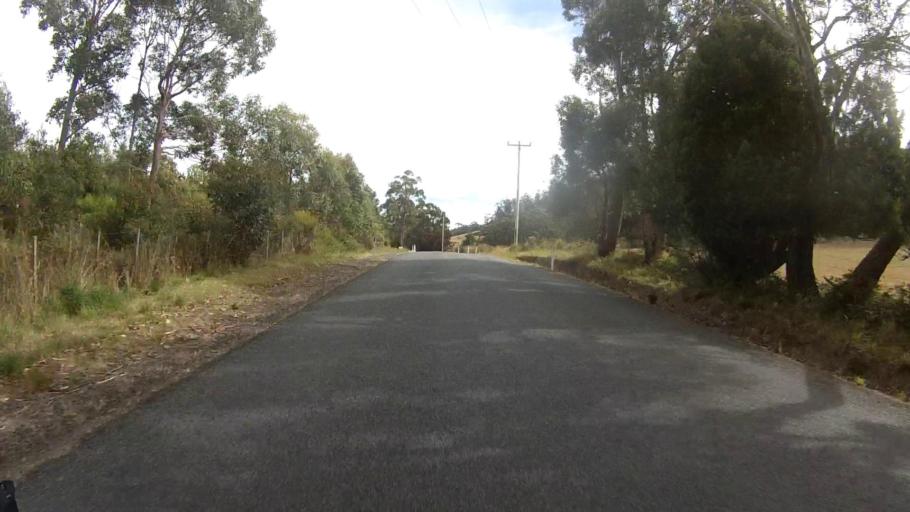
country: AU
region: Tasmania
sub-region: Sorell
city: Sorell
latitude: -42.8098
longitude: 147.7945
